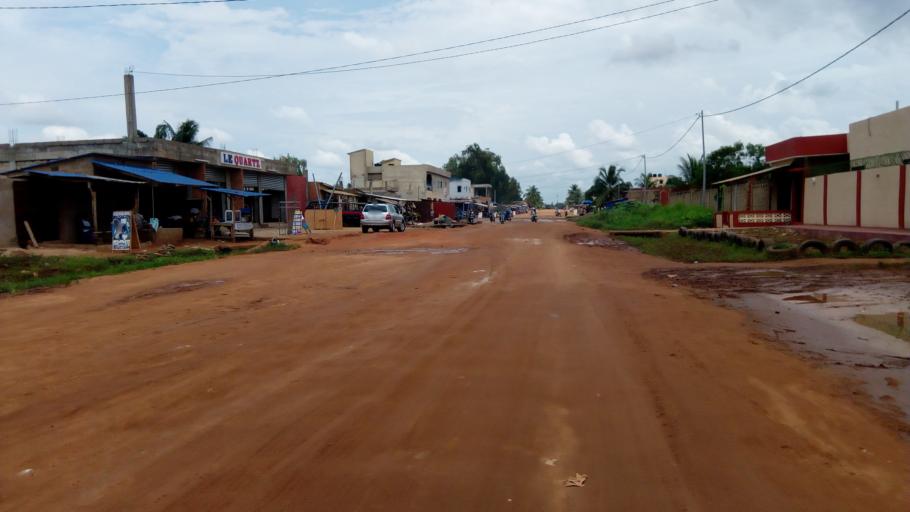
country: TG
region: Maritime
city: Lome
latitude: 6.2249
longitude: 1.1616
